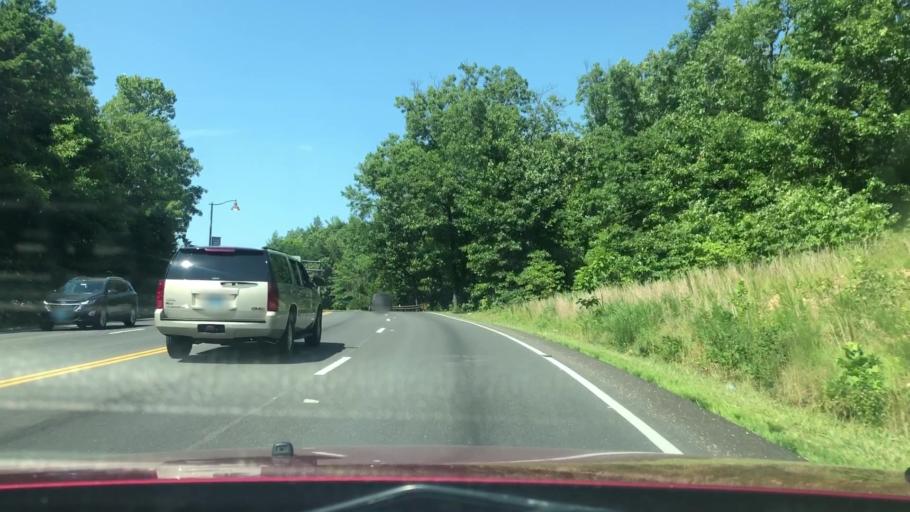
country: US
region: Missouri
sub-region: Stone County
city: Kimberling City
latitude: 36.6690
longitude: -93.3355
